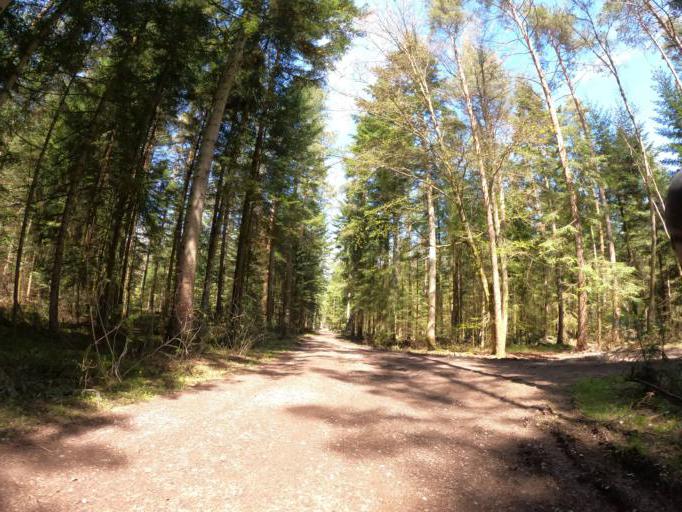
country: DE
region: Baden-Wuerttemberg
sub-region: Karlsruhe Region
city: Oberreichenbach
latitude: 48.7222
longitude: 8.6595
